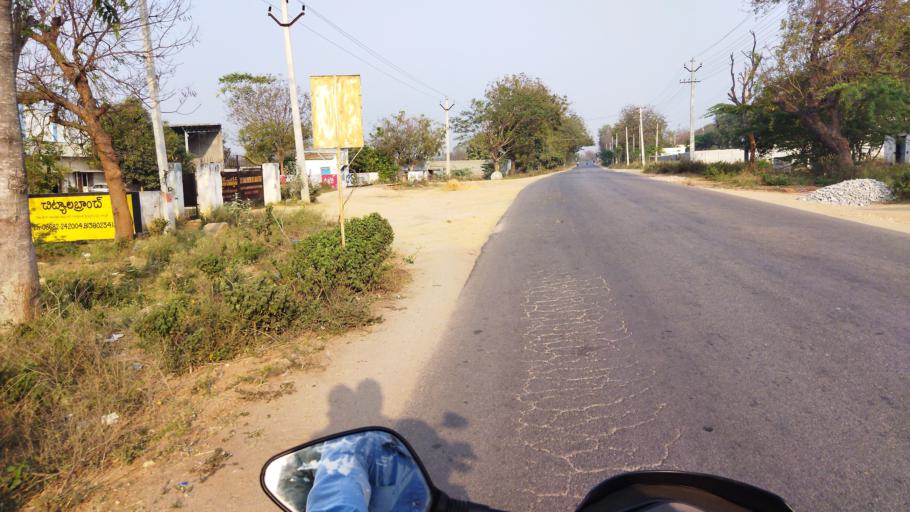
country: IN
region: Telangana
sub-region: Nalgonda
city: Nalgonda
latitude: 17.2387
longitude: 79.1182
